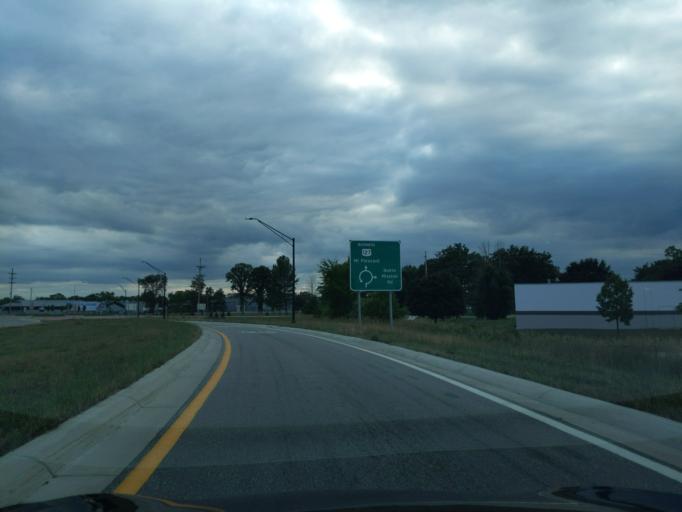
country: US
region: Michigan
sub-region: Isabella County
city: Mount Pleasant
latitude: 43.6181
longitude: -84.7662
